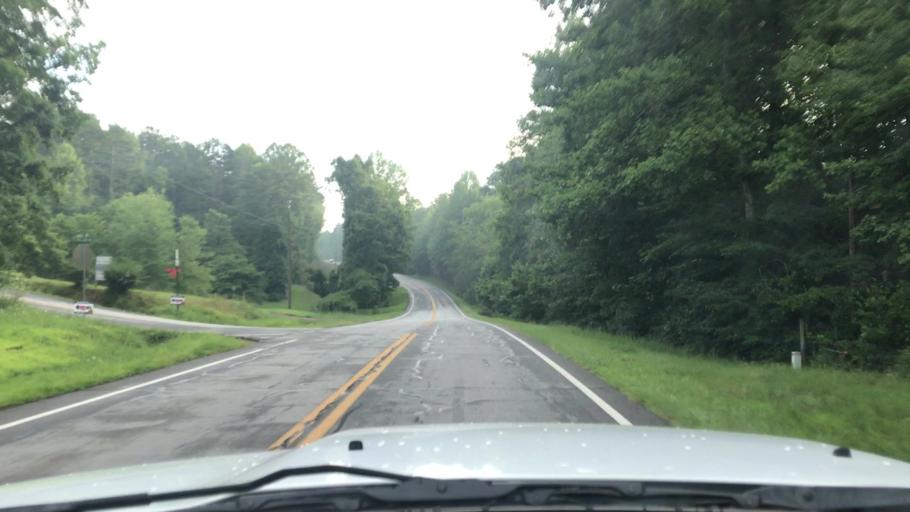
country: US
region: Georgia
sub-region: Fannin County
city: Blue Ridge
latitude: 34.9619
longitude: -84.2234
